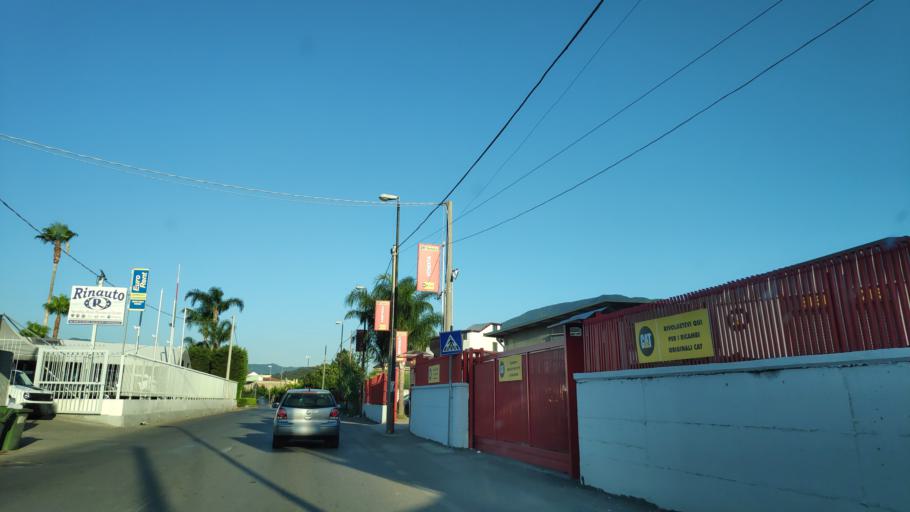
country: IT
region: Campania
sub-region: Provincia di Salerno
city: Pagani
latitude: 40.7635
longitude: 14.6119
